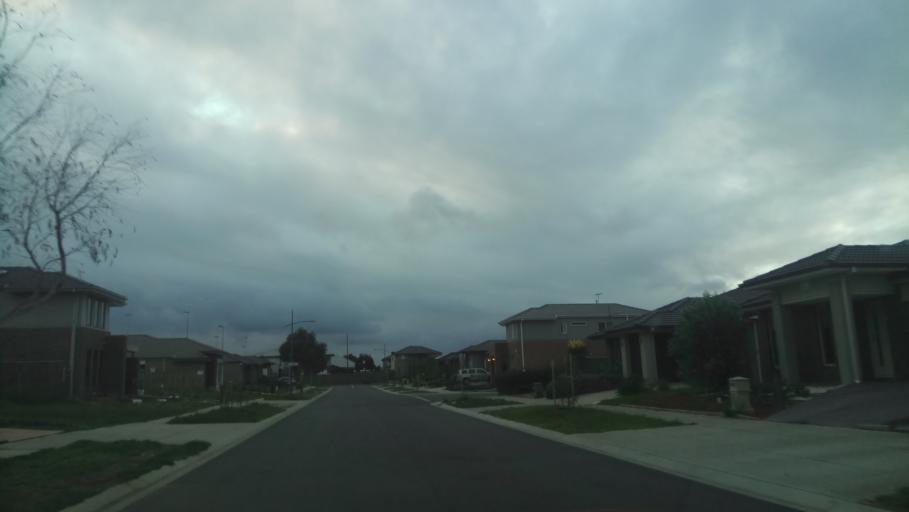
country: AU
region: Victoria
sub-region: Wyndham
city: Point Cook
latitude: -37.9068
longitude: 144.7607
